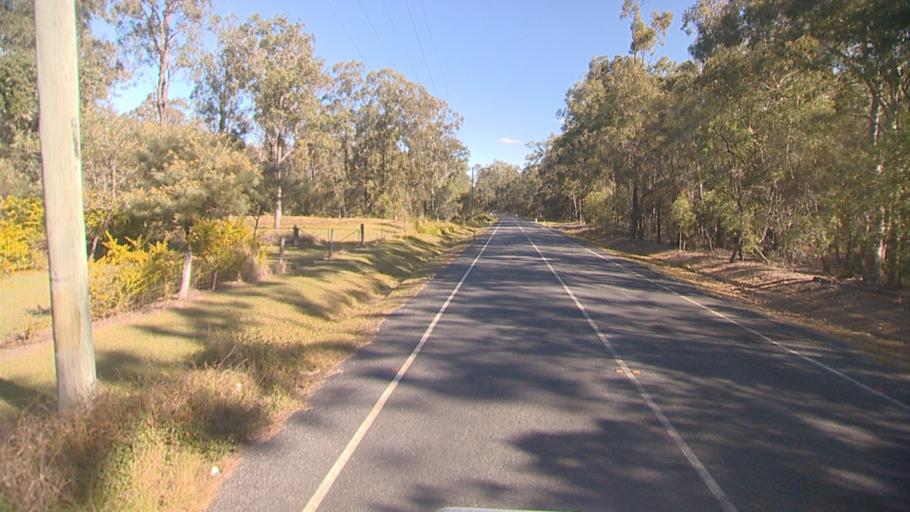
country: AU
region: Queensland
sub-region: Logan
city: North Maclean
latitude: -27.8076
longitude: 153.0600
